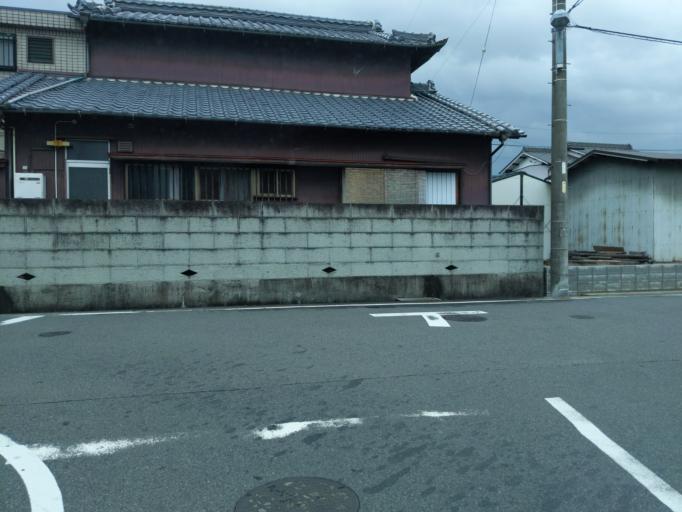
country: JP
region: Aichi
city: Kasugai
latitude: 35.2605
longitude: 136.9893
